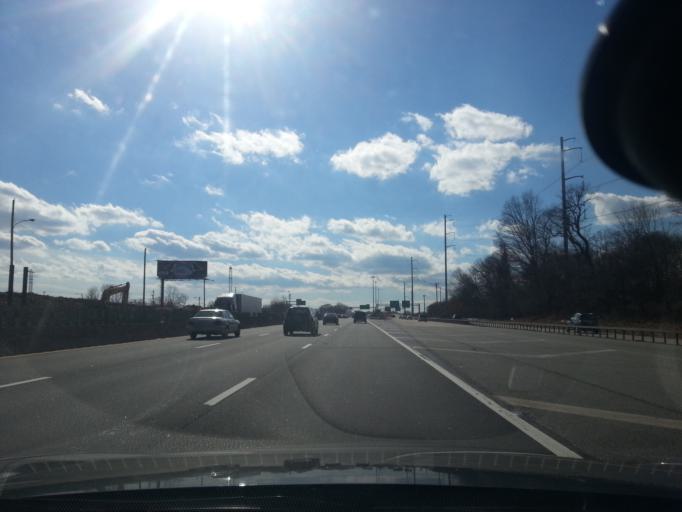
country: US
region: Pennsylvania
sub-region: Delaware County
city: Upland
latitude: 39.8498
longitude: -75.3794
